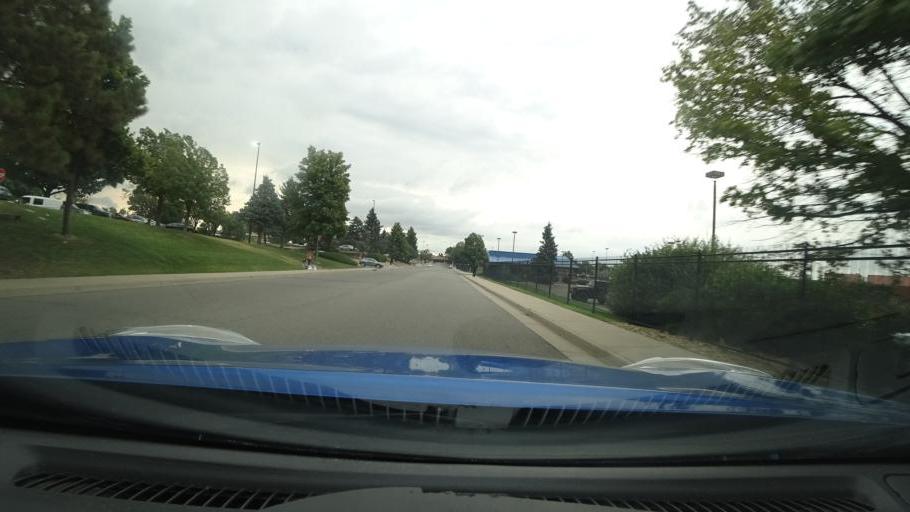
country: US
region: Colorado
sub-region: Adams County
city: Aurora
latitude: 39.7023
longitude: -104.8250
